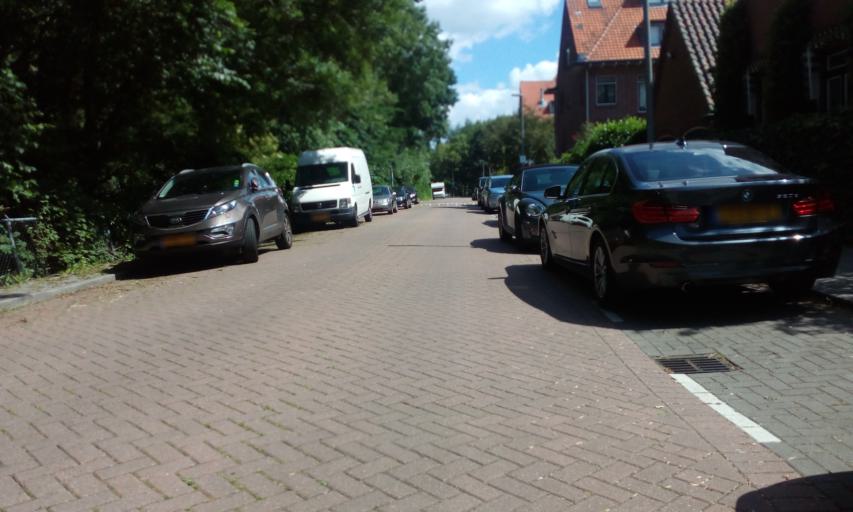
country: NL
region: South Holland
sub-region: Gemeente Lansingerland
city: Bergschenhoek
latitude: 51.9575
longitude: 4.4846
